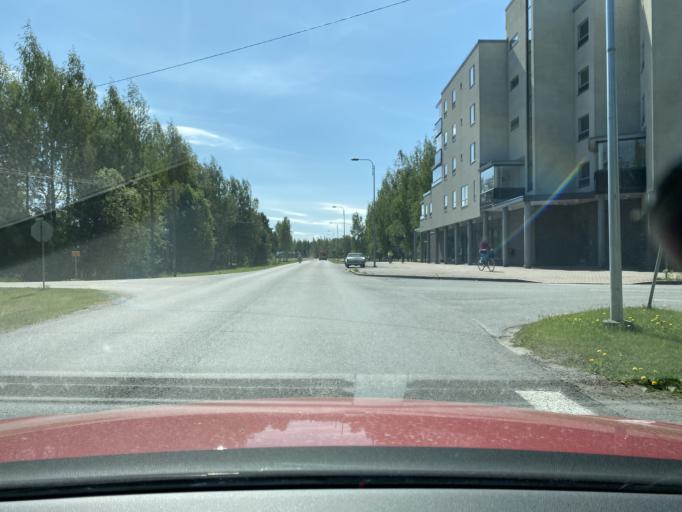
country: FI
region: Satakunta
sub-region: Rauma
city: Eura
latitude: 61.1291
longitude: 22.1443
